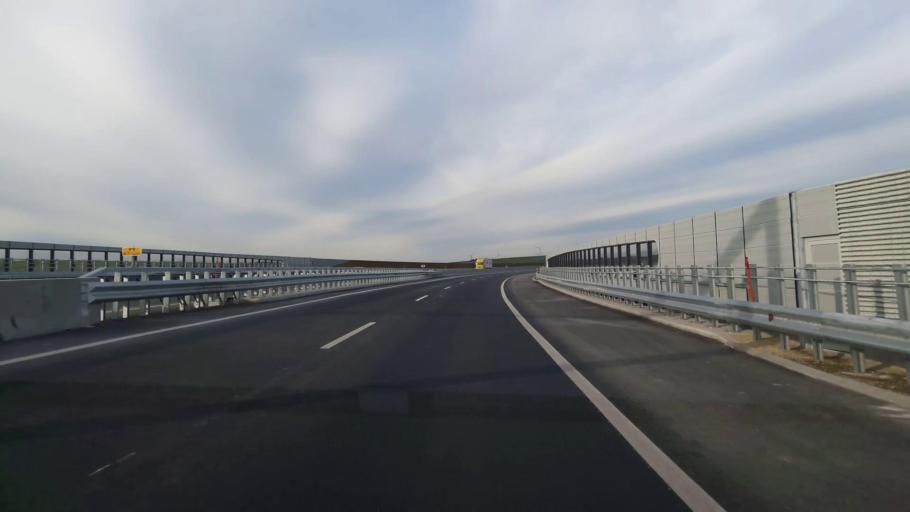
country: AT
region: Lower Austria
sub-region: Politischer Bezirk Mistelbach
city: Wilfersdorf
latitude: 48.5755
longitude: 16.6252
